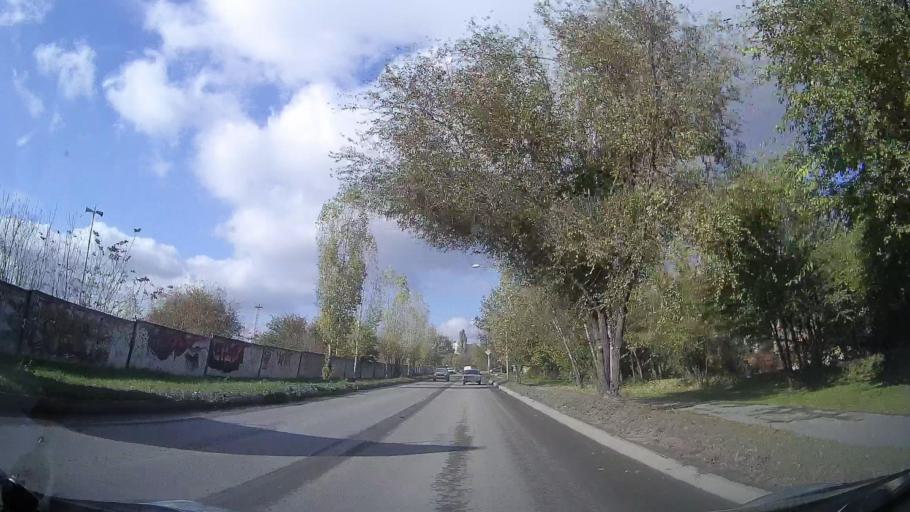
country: RU
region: Rostov
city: Rostov-na-Donu
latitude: 47.2252
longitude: 39.6838
